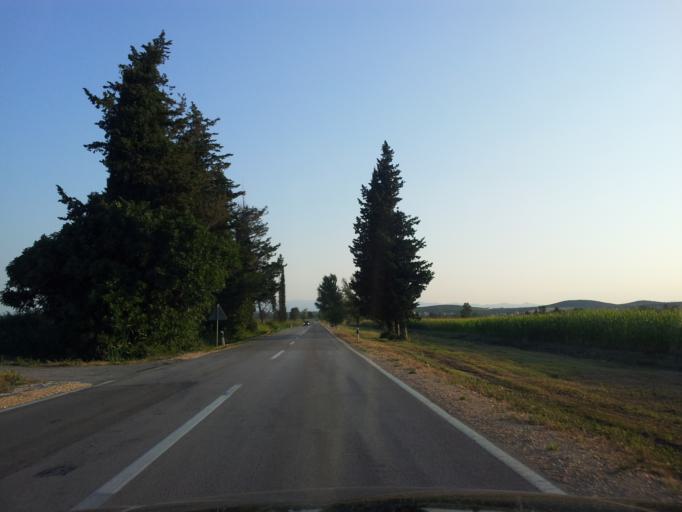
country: HR
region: Zadarska
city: Biograd na Moru
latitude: 43.9685
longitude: 15.4842
